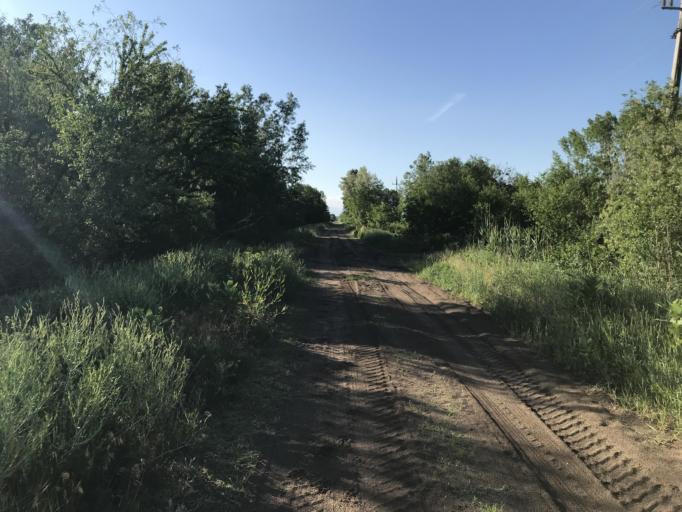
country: HU
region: Bacs-Kiskun
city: Tiszakecske
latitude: 46.9665
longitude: 20.0707
